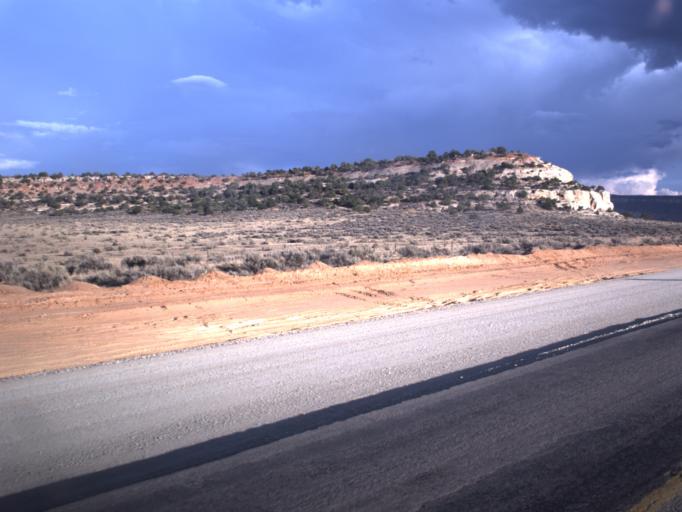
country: US
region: Utah
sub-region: San Juan County
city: Monticello
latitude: 38.1050
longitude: -109.3624
